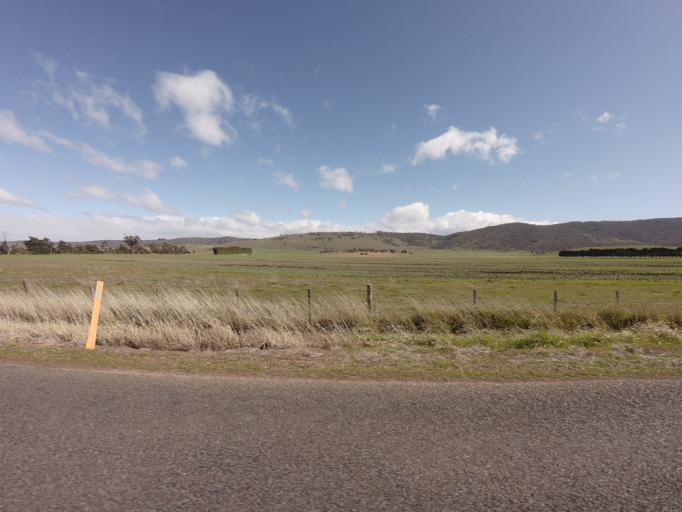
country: AU
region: Tasmania
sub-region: Northern Midlands
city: Evandale
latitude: -41.9972
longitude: 147.4550
